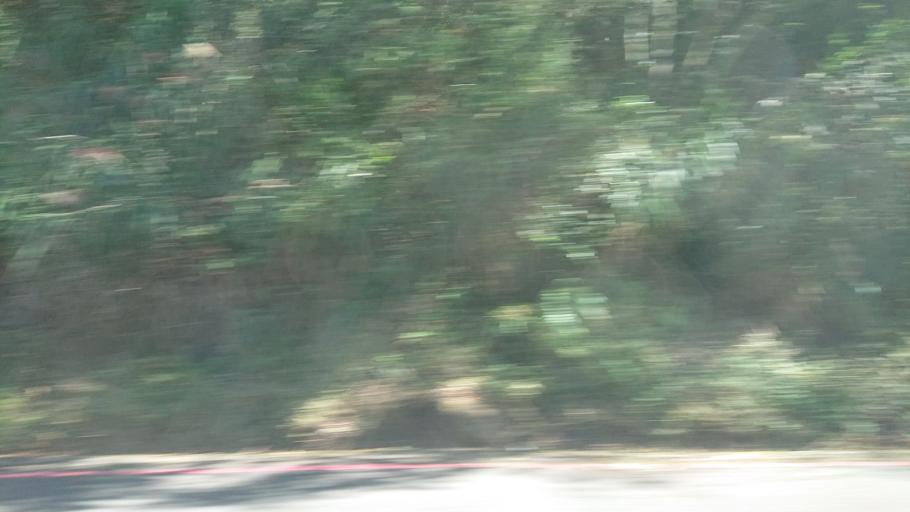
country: TW
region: Taiwan
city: Lugu
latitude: 23.5022
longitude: 120.7997
